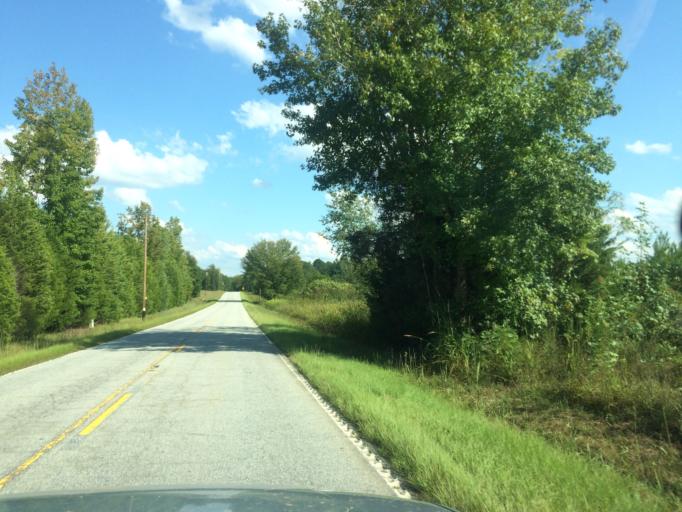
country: US
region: South Carolina
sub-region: Greenwood County
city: Ware Shoals
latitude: 34.4648
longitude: -82.1761
